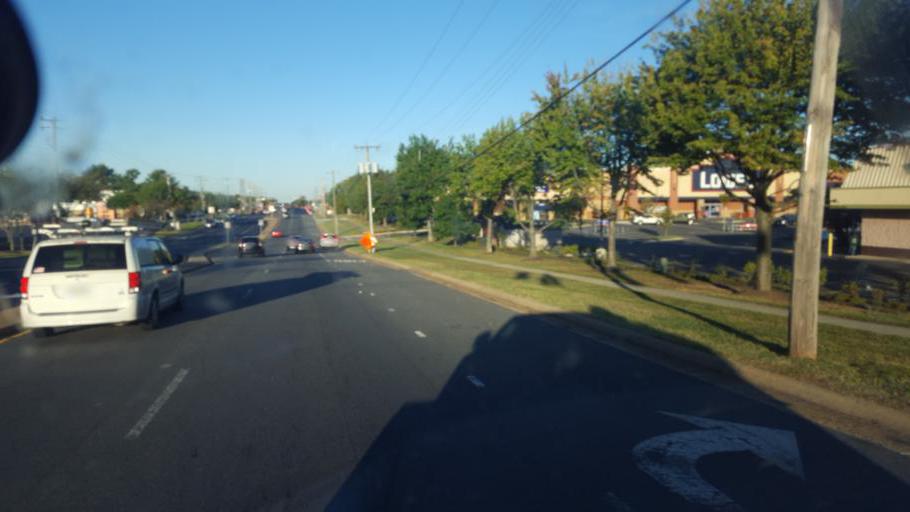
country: US
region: Virginia
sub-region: City of Fairfax
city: Fairfax
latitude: 38.8518
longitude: -77.3324
